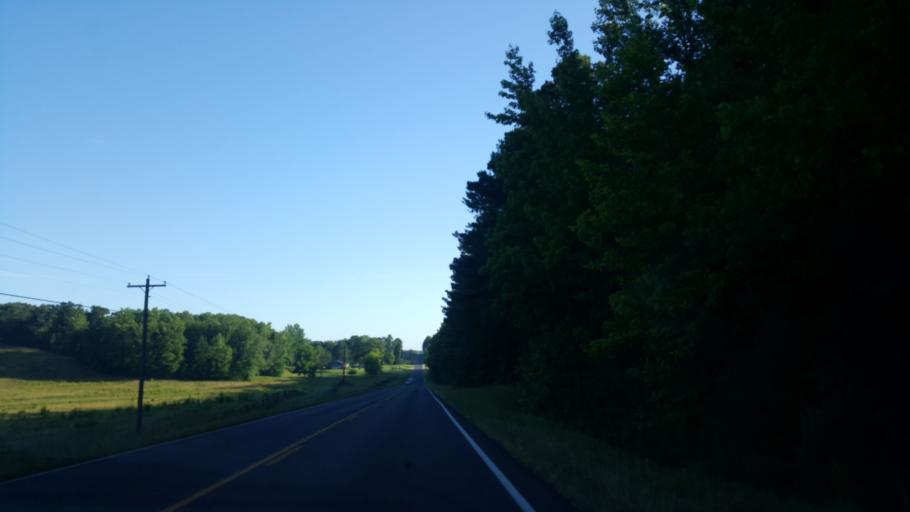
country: US
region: Tennessee
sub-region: Henderson County
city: Lexington
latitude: 35.5529
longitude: -88.3851
